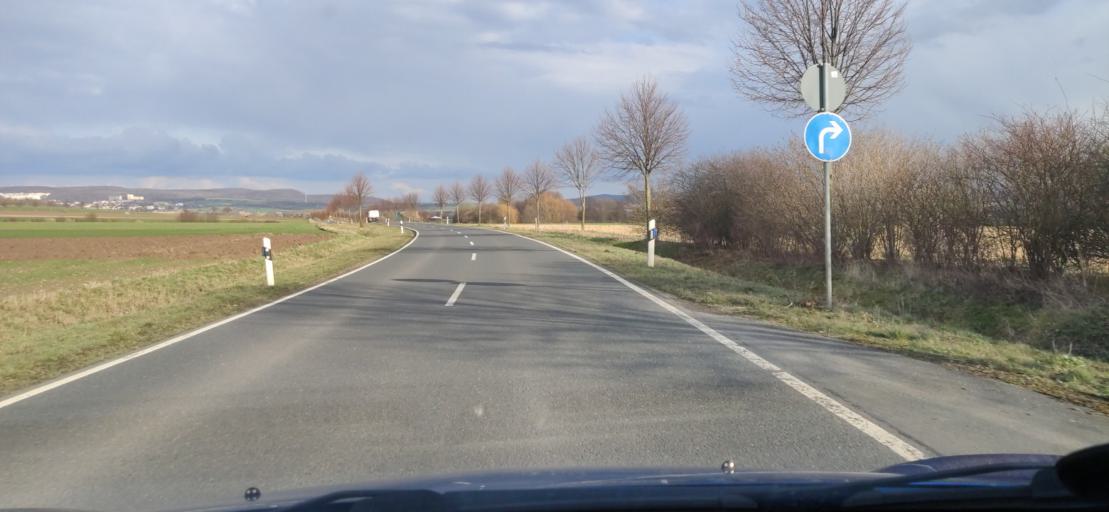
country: DE
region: Lower Saxony
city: Rosdorf
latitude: 51.4904
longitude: 9.8835
